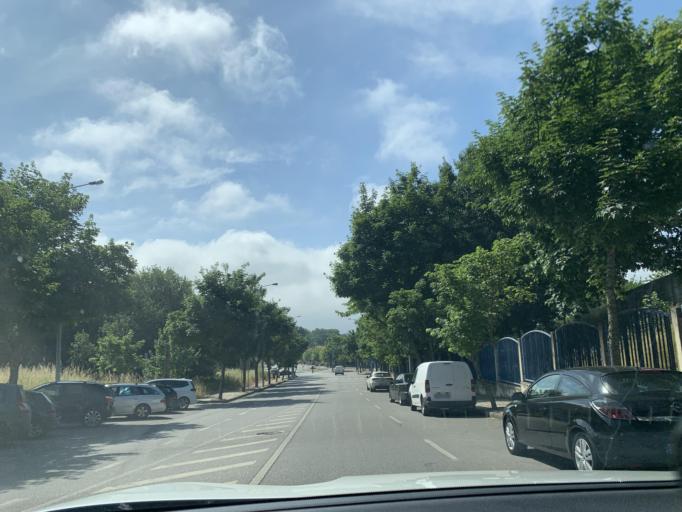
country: PT
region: Viseu
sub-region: Viseu
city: Viseu
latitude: 40.6511
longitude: -7.9042
